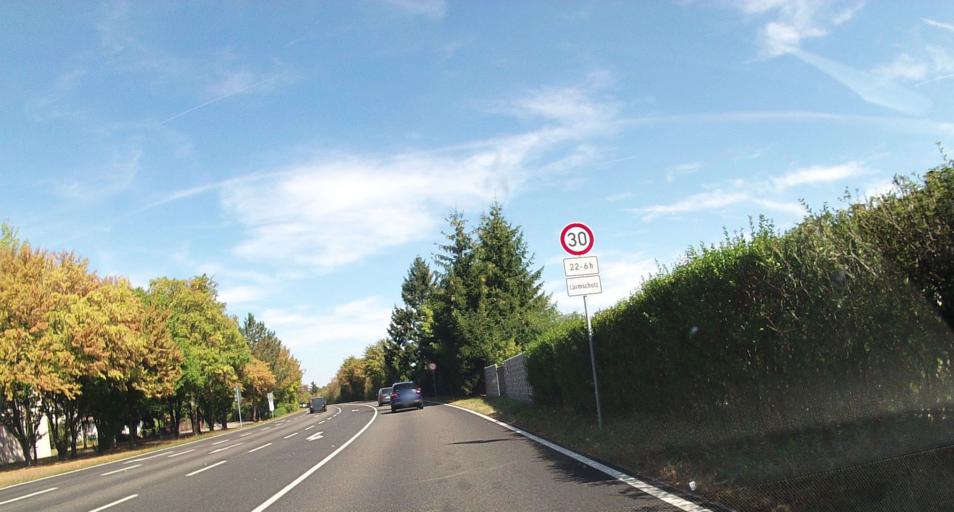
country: DE
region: Baden-Wuerttemberg
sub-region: Karlsruhe Region
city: Rastatt
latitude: 48.8387
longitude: 8.2028
